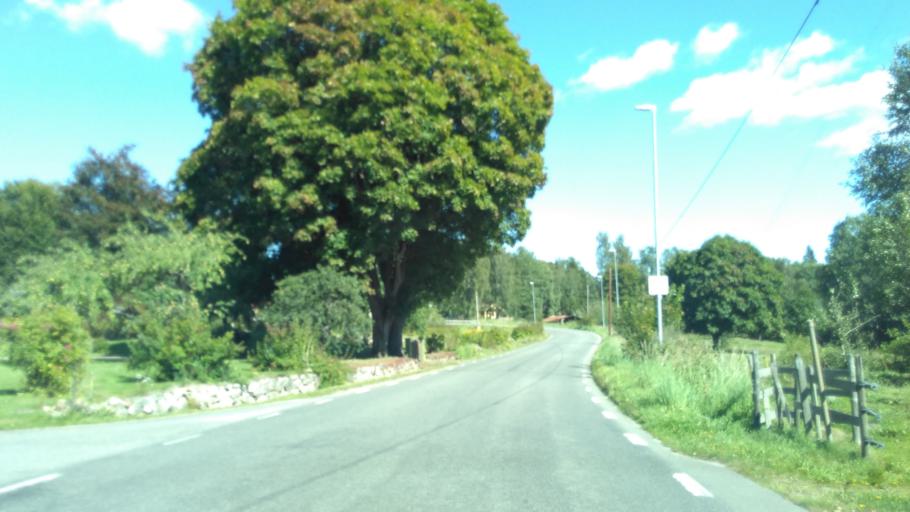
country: SE
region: Vaestra Goetaland
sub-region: Skara Kommun
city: Axvall
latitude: 58.4150
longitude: 13.6090
